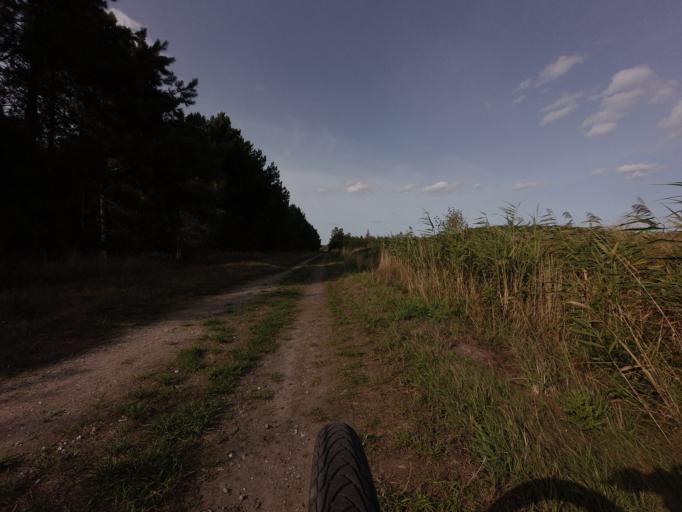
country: DK
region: Zealand
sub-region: Vordingborg Kommune
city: Praesto
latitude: 55.1401
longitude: 12.0898
